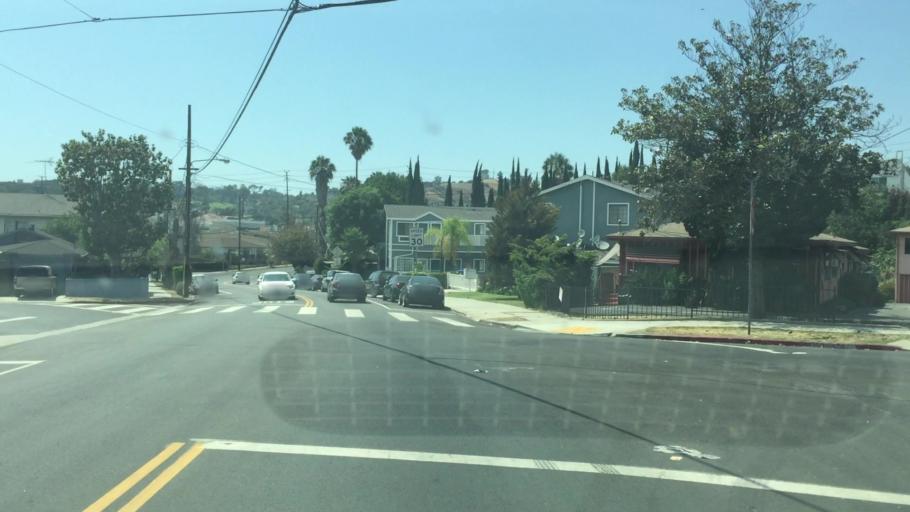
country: US
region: California
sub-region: Los Angeles County
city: Glendale
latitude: 34.1210
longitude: -118.2222
